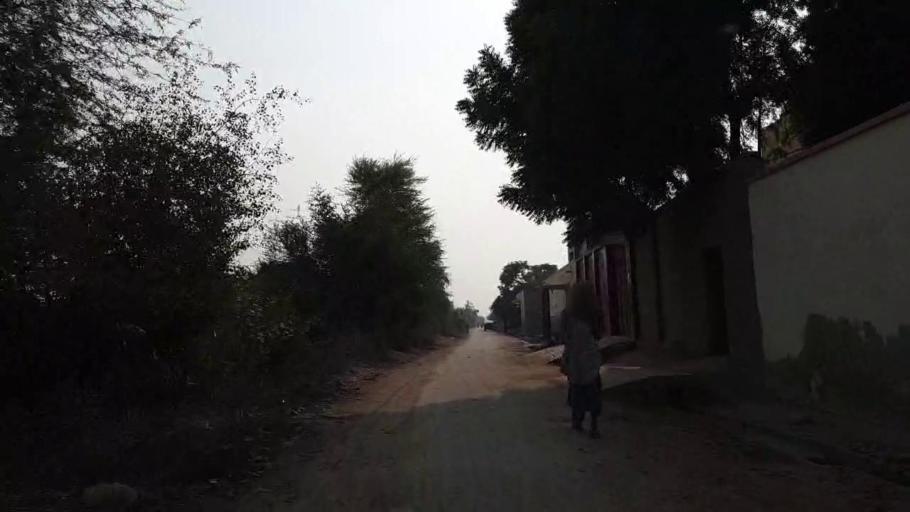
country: PK
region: Sindh
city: Bhan
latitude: 26.5776
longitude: 67.7293
